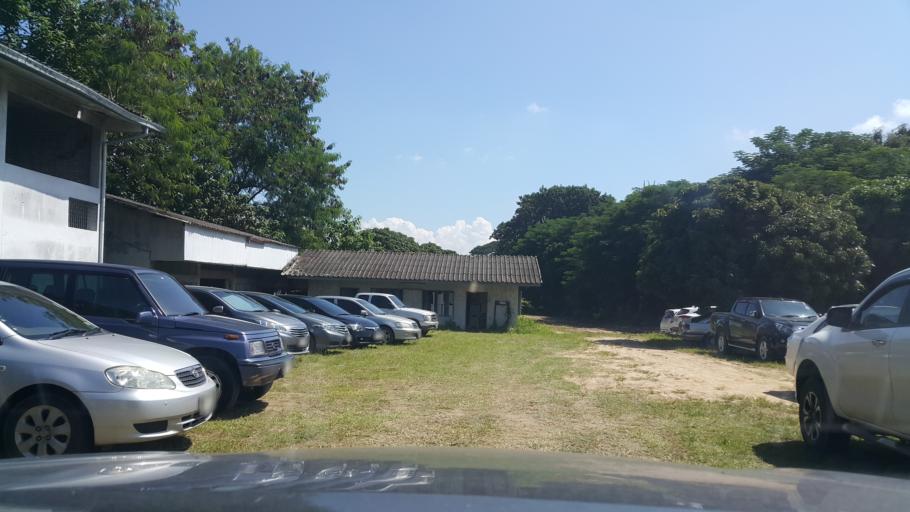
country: TH
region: Chiang Mai
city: San Sai
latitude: 18.9136
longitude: 98.9687
